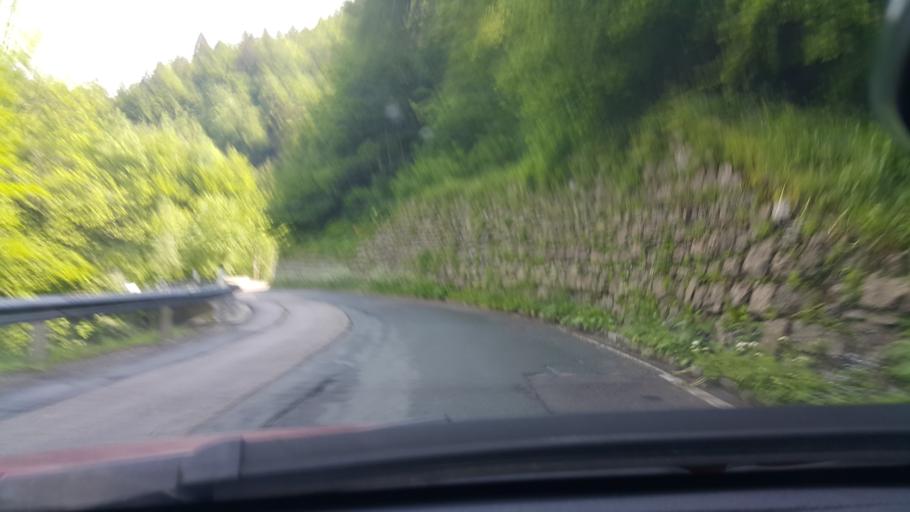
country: AT
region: Carinthia
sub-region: Politischer Bezirk Klagenfurt Land
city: Ferlach
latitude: 46.4713
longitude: 14.2587
